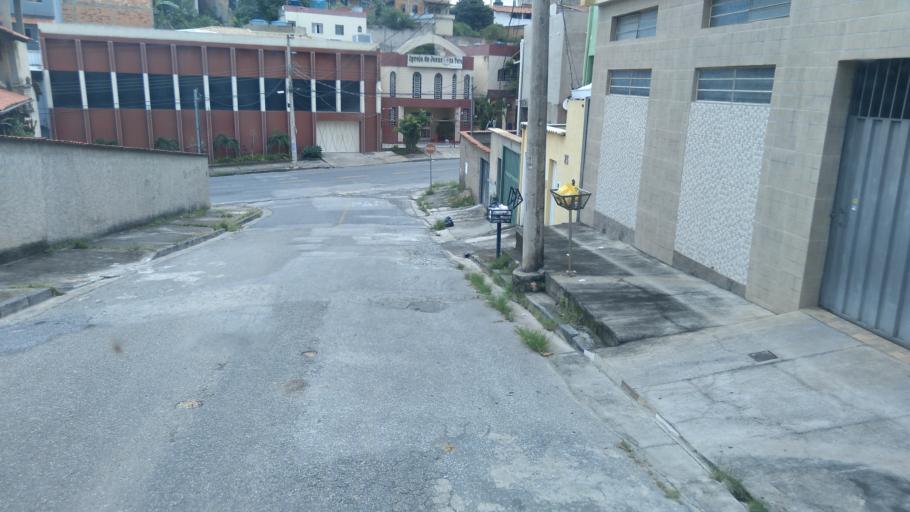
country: BR
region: Minas Gerais
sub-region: Belo Horizonte
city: Belo Horizonte
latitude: -19.8492
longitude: -43.9083
